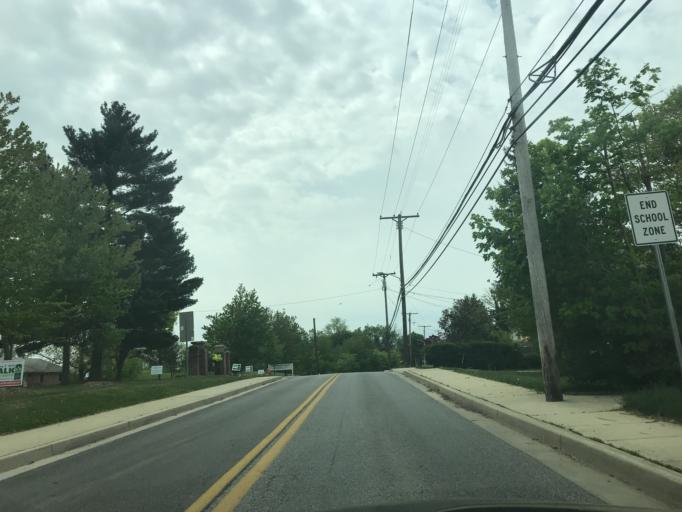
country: US
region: Maryland
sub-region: Baltimore County
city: Catonsville
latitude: 39.2670
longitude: -76.7298
